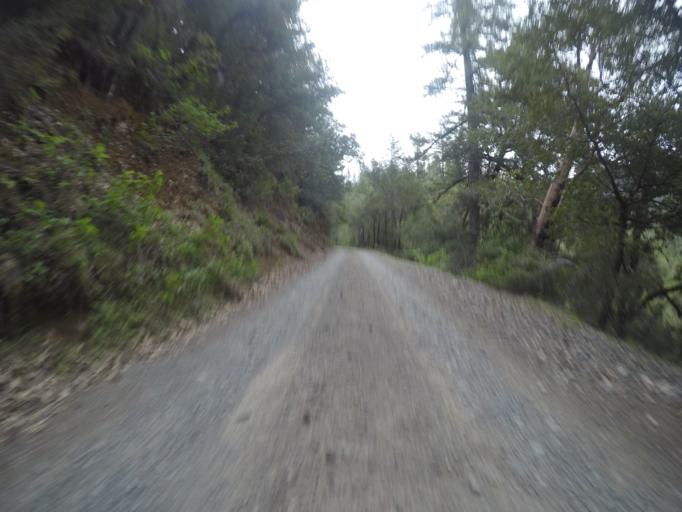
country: US
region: California
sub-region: Del Norte County
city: Bertsch-Oceanview
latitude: 41.7384
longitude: -123.8789
